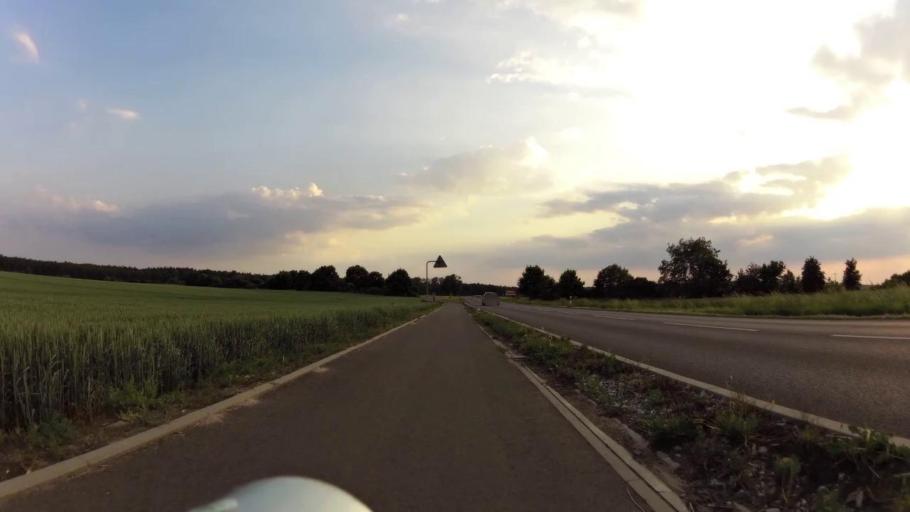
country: PL
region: Kujawsko-Pomorskie
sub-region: Powiat chelminski
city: Unislaw
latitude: 53.1988
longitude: 18.3621
